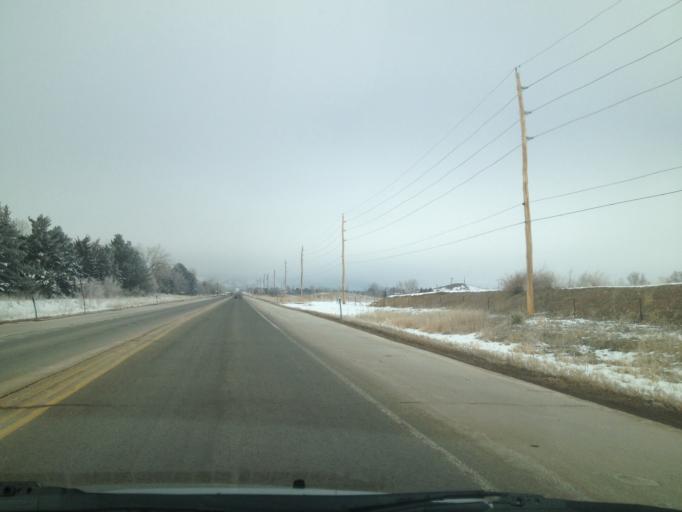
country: US
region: Colorado
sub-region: Boulder County
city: Boulder
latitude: 40.0559
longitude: -105.2669
